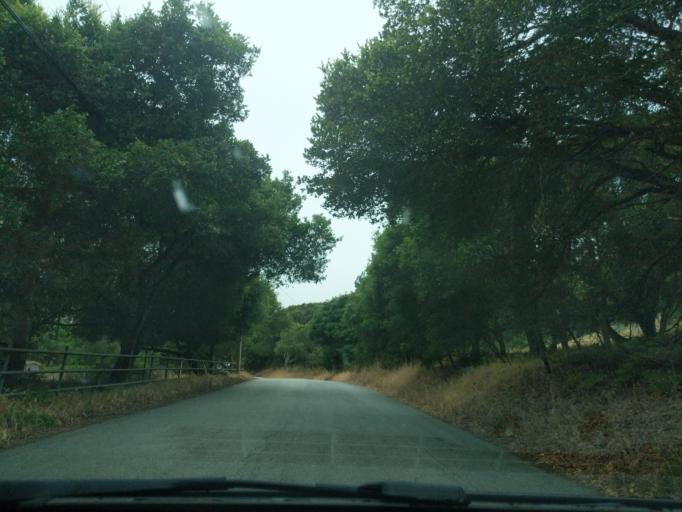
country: US
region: California
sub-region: San Benito County
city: Aromas
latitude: 36.8873
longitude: -121.6176
